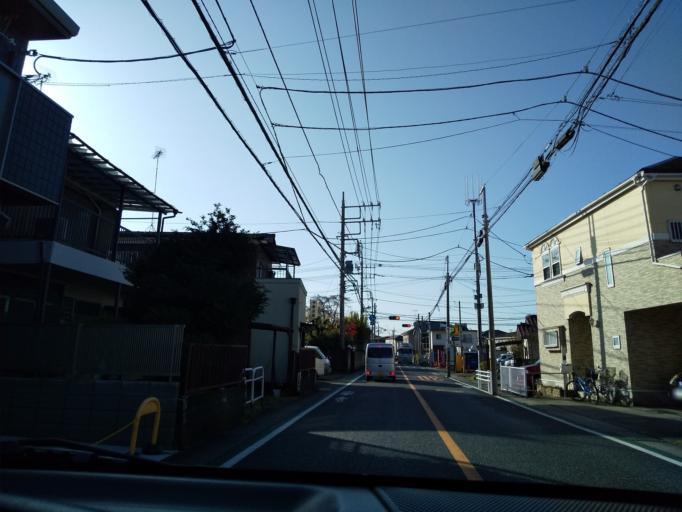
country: JP
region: Tokyo
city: Hino
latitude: 35.6944
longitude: 139.3995
